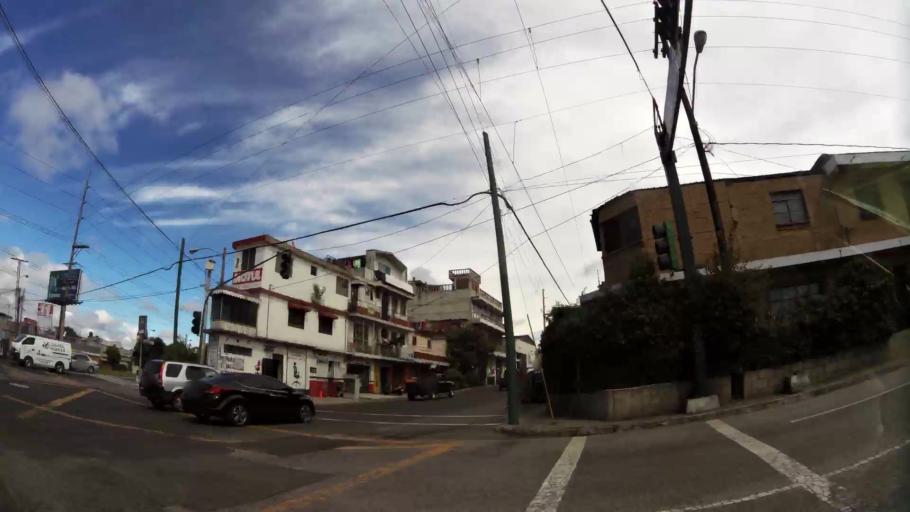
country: GT
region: Guatemala
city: Guatemala City
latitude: 14.6015
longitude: -90.5391
